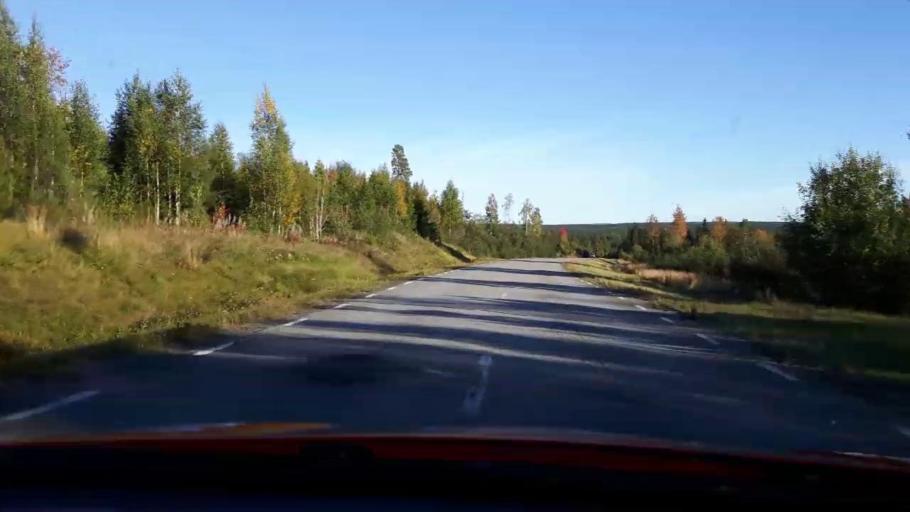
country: SE
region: Jaemtland
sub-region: OEstersunds Kommun
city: Lit
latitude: 63.7461
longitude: 14.7249
